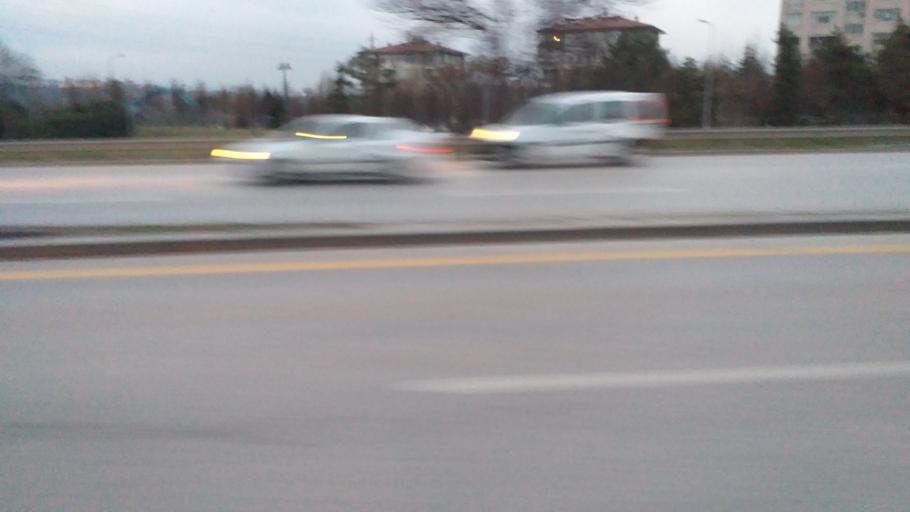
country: TR
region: Ankara
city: Ankara
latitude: 39.9558
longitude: 32.8192
